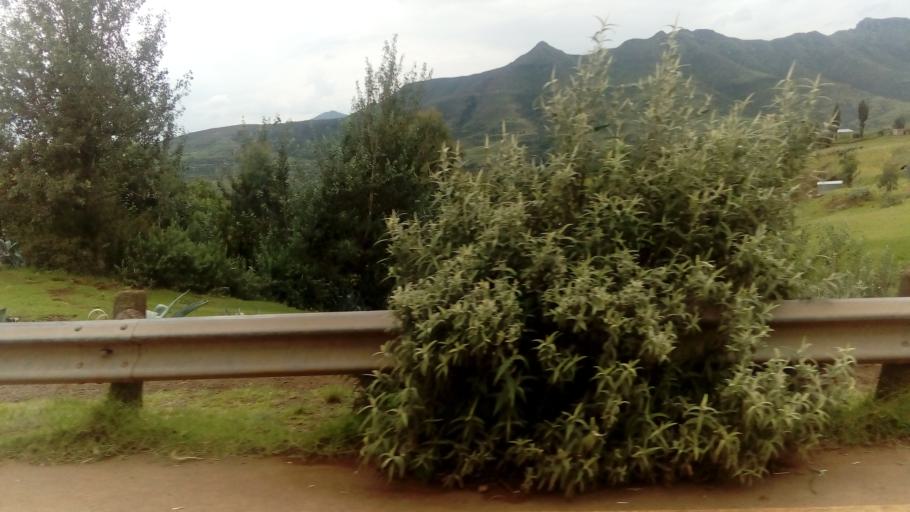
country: LS
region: Butha-Buthe
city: Butha-Buthe
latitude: -29.0328
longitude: 28.2687
